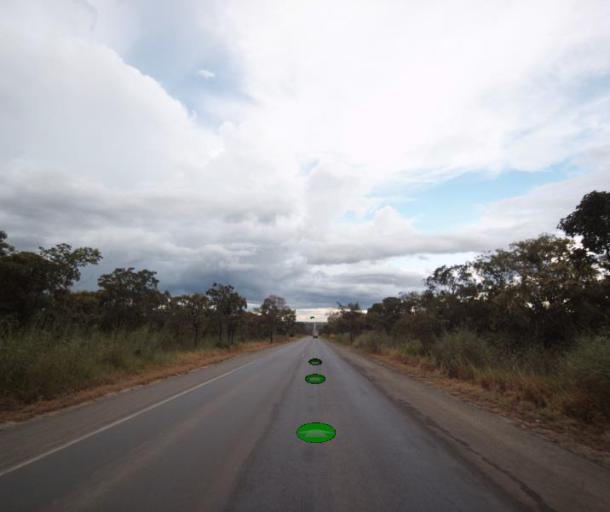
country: BR
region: Goias
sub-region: Itapaci
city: Itapaci
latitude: -14.8290
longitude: -49.3030
